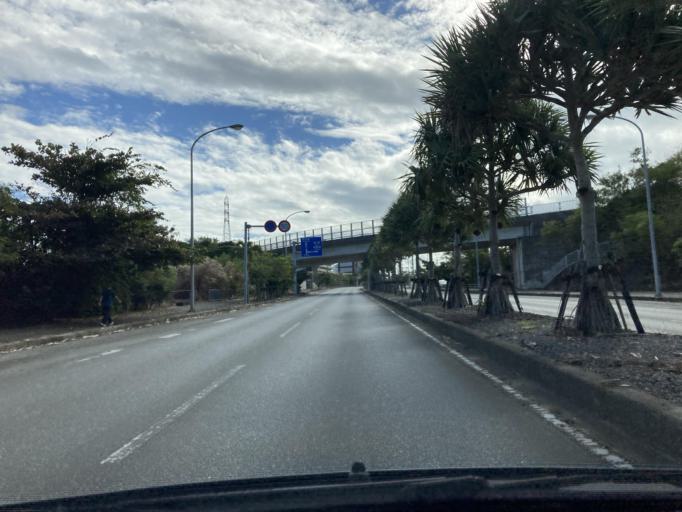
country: JP
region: Okinawa
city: Tomigusuku
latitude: 26.1667
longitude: 127.7256
